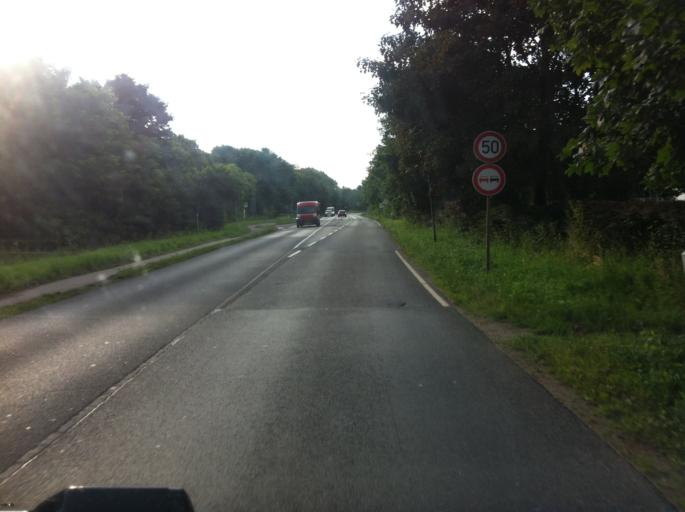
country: DE
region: North Rhine-Westphalia
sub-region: Regierungsbezirk Koln
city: Mengenich
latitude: 50.9762
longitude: 6.8570
